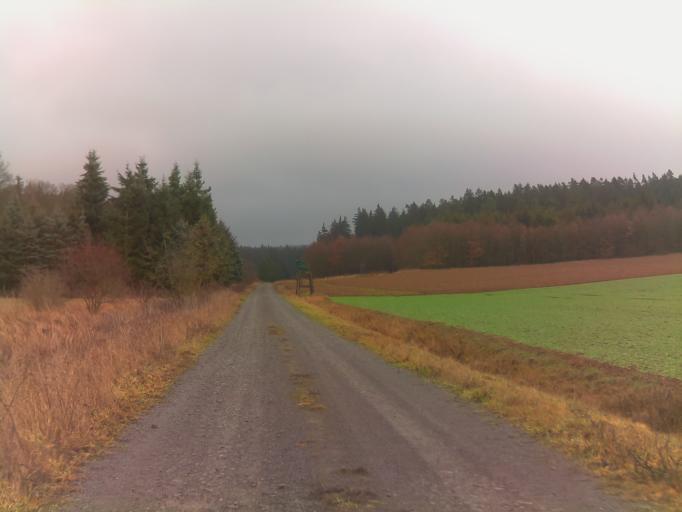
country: DE
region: Thuringia
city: Juchsen
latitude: 50.4603
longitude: 10.4716
